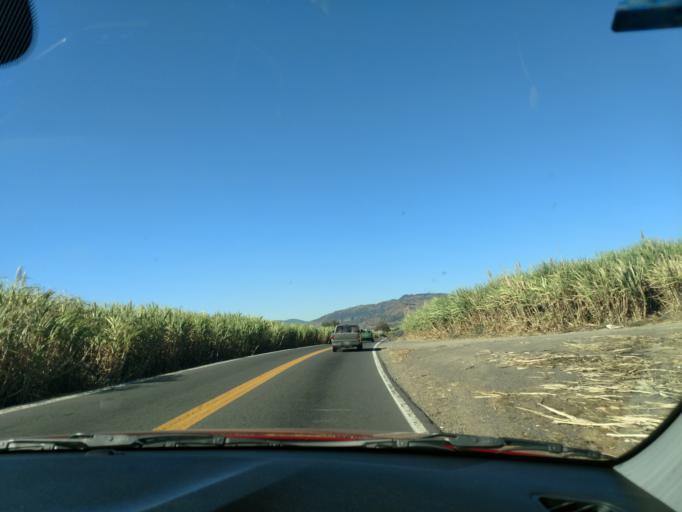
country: MX
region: Nayarit
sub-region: Ahuacatlan
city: Ahuacatlan
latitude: 21.1338
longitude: -104.6063
